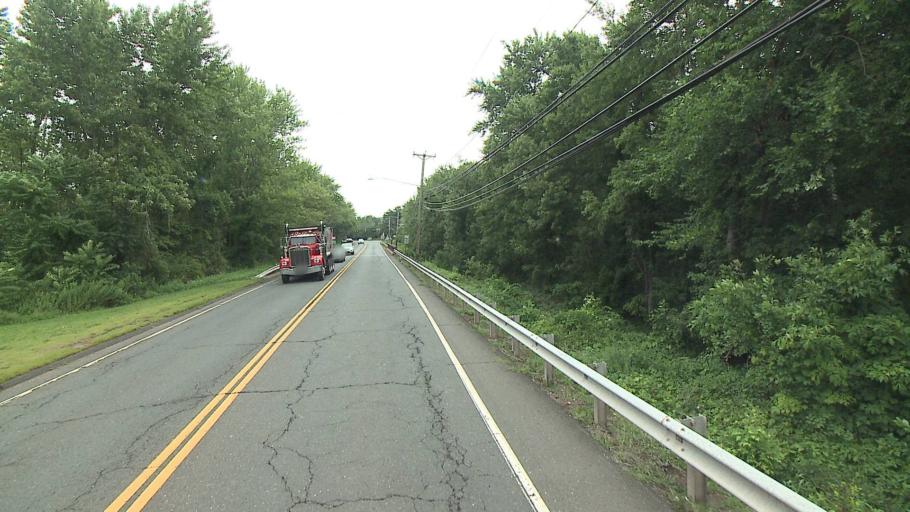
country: US
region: Connecticut
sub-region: Middlesex County
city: Cromwell
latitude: 41.5972
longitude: -72.6770
